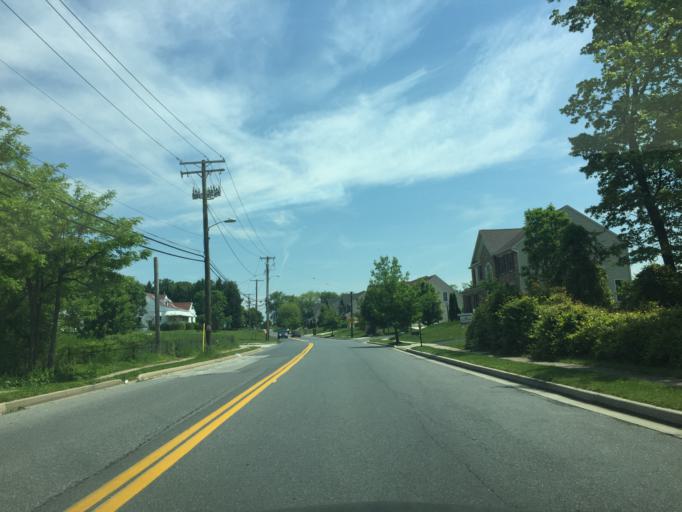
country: US
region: Maryland
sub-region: Baltimore County
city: Carney
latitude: 39.3960
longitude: -76.5108
